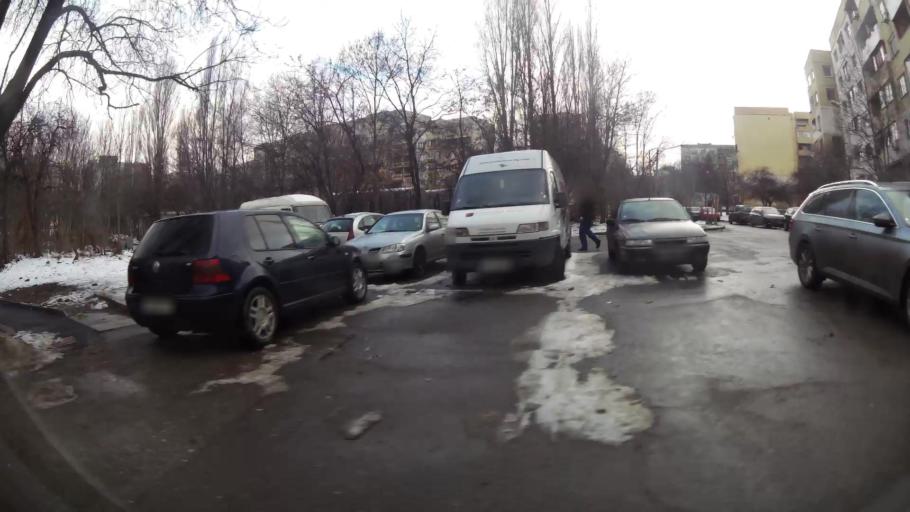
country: BG
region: Sofia-Capital
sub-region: Stolichna Obshtina
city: Sofia
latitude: 42.7077
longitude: 23.2951
